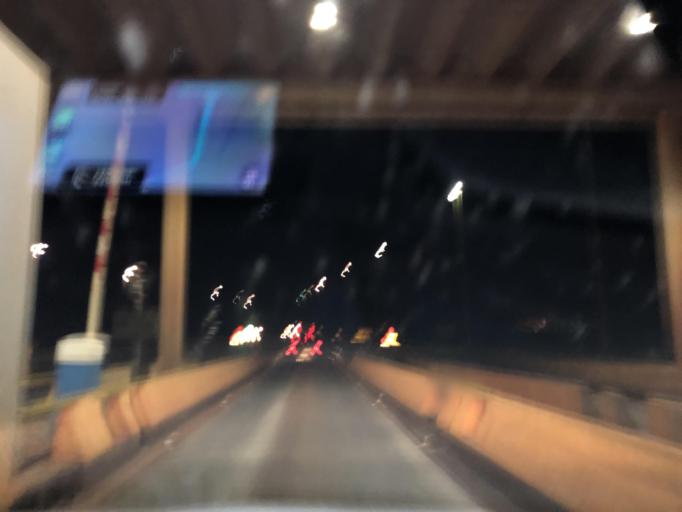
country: BR
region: Goias
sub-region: Cristalina
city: Cristalina
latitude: -16.7389
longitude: -47.6173
